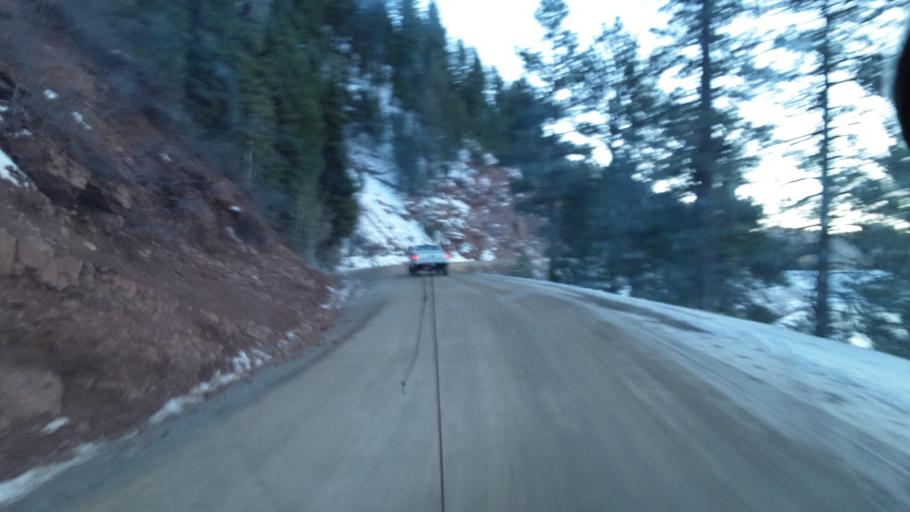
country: US
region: Colorado
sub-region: La Plata County
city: Bayfield
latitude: 37.3880
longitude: -107.6569
